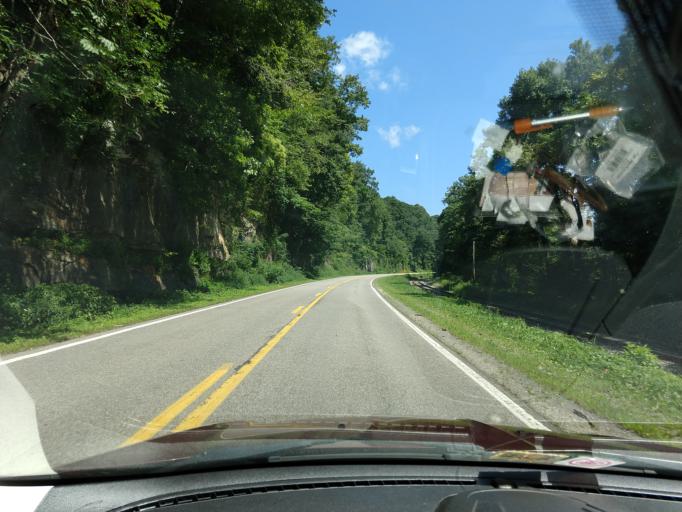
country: US
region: West Virginia
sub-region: Kanawha County
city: Montgomery
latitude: 38.1329
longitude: -81.2202
